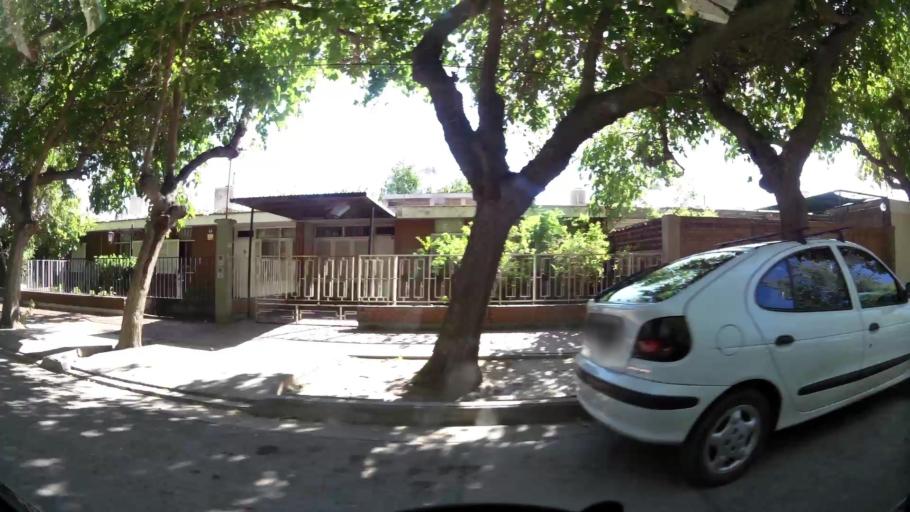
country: AR
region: San Juan
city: San Juan
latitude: -31.5270
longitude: -68.5361
